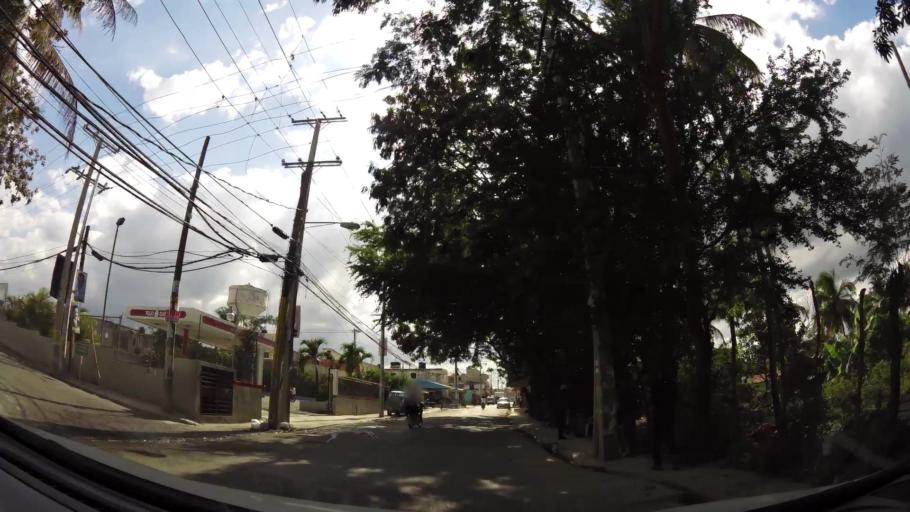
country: DO
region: Nacional
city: Ensanche Luperon
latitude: 18.5430
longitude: -69.8931
